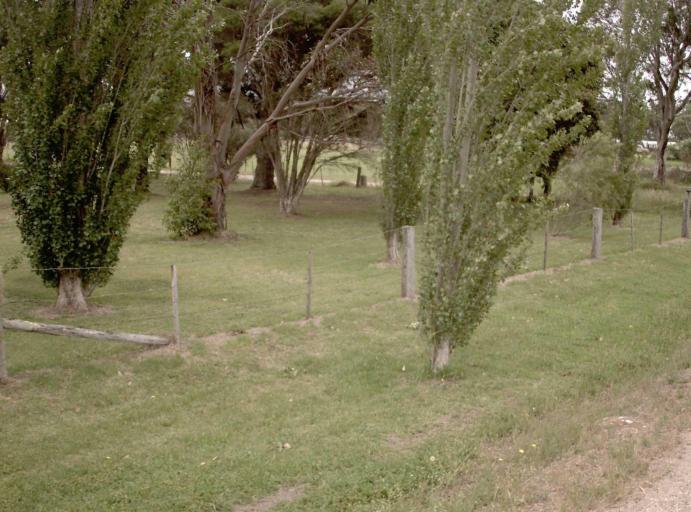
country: AU
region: Victoria
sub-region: East Gippsland
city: Bairnsdale
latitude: -37.8297
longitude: 147.4336
